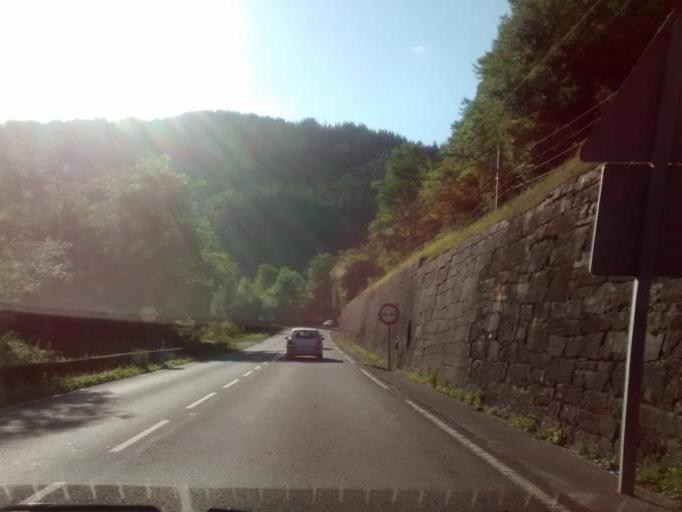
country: ES
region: Basque Country
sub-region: Provincia de Guipuzcoa
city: Elgoibar
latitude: 43.2324
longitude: -2.4012
